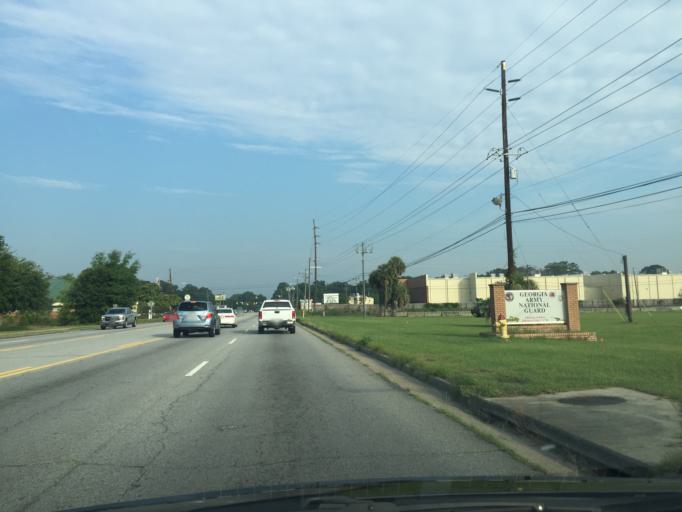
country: US
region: Georgia
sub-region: Chatham County
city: Isle of Hope
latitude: 32.0057
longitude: -81.0973
